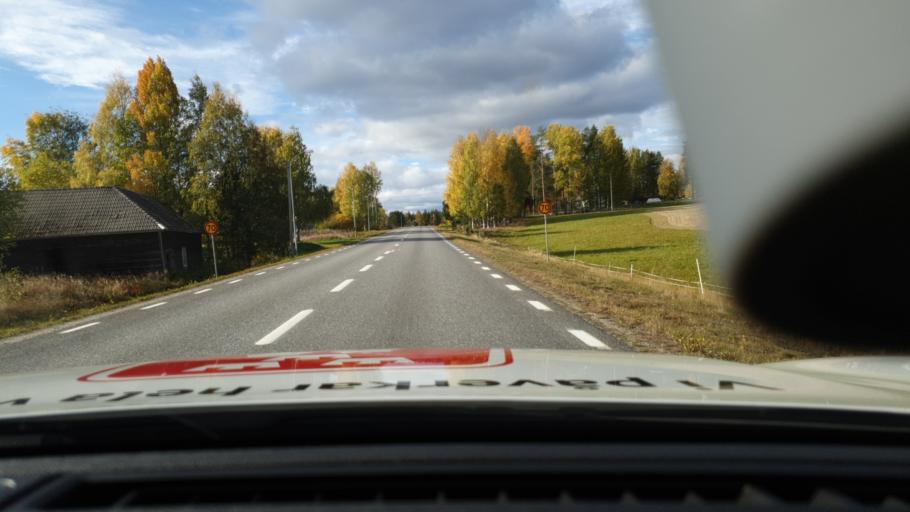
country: SE
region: Vaesterbotten
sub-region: Mala Kommun
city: Mala
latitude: 64.9886
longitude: 18.5038
